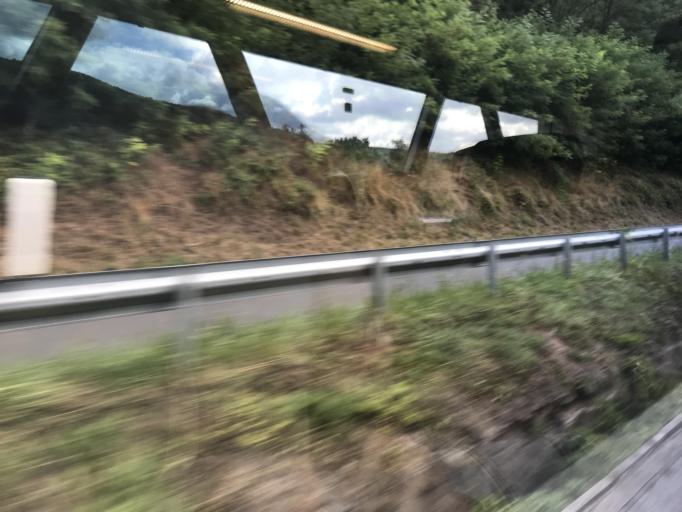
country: DE
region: Bavaria
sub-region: Regierungsbezirk Unterfranken
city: Grafendorf
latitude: 50.1271
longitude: 9.7583
